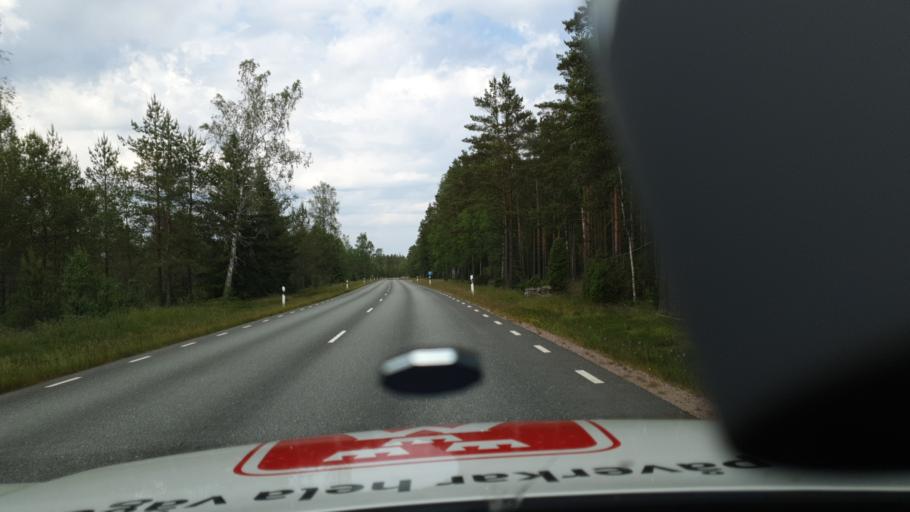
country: SE
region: Joenkoeping
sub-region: Vaggeryds Kommun
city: Skillingaryd
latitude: 57.3148
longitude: 14.0912
